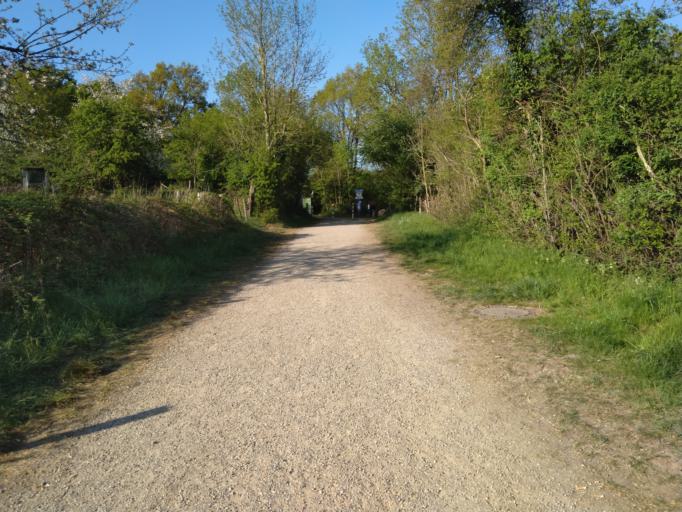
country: DE
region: North Rhine-Westphalia
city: Stolberg
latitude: 50.7450
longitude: 6.1777
